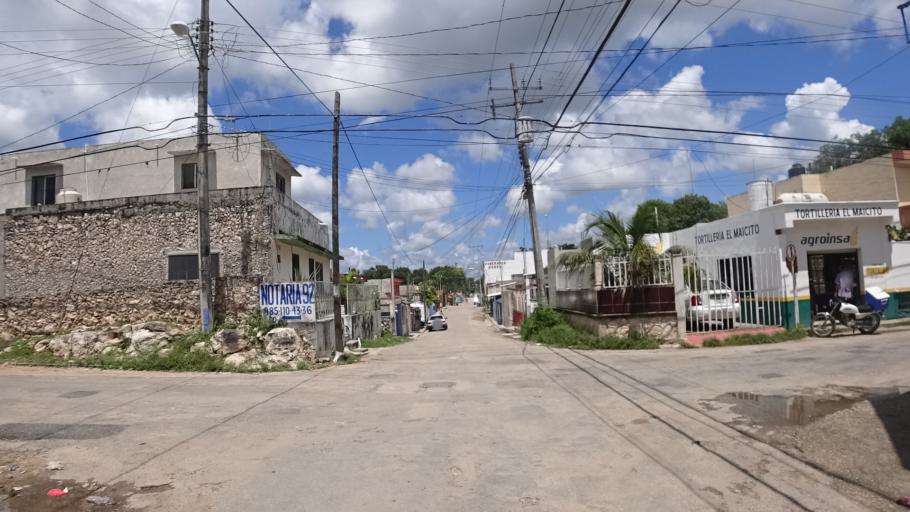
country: MX
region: Yucatan
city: Valladolid
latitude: 20.6869
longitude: -88.2124
